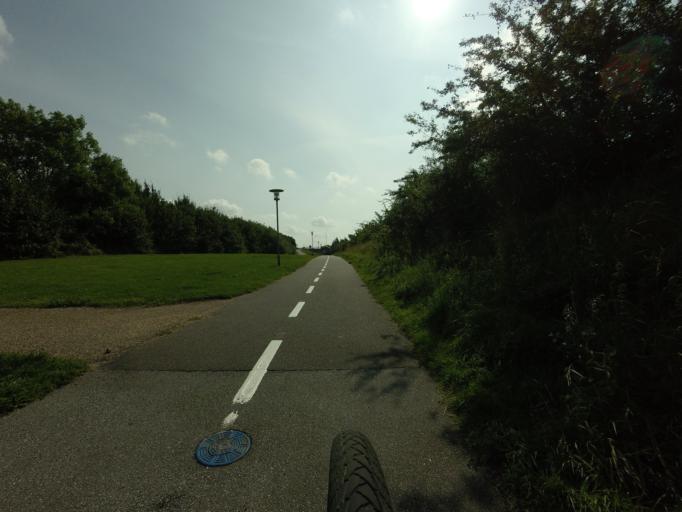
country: DK
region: Zealand
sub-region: Naestved Kommune
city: Naestved
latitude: 55.2242
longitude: 11.7799
